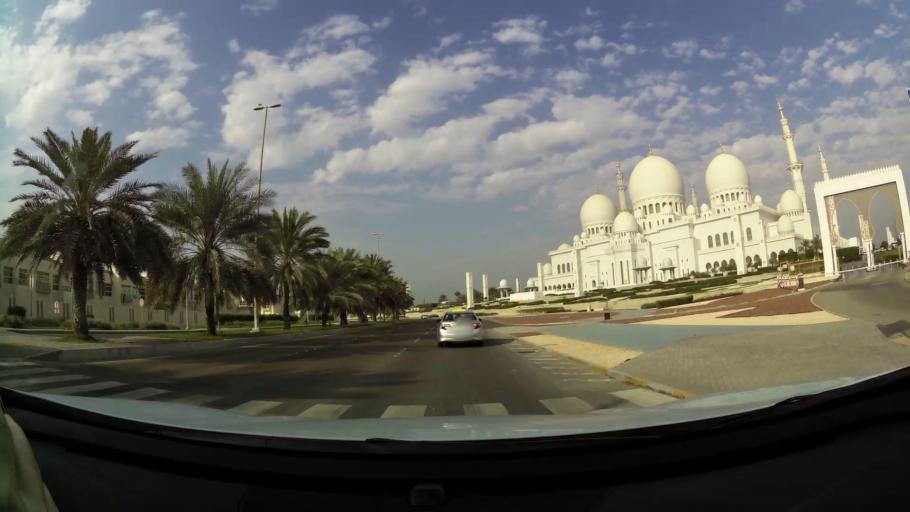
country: AE
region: Abu Dhabi
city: Abu Dhabi
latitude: 24.4110
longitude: 54.4725
